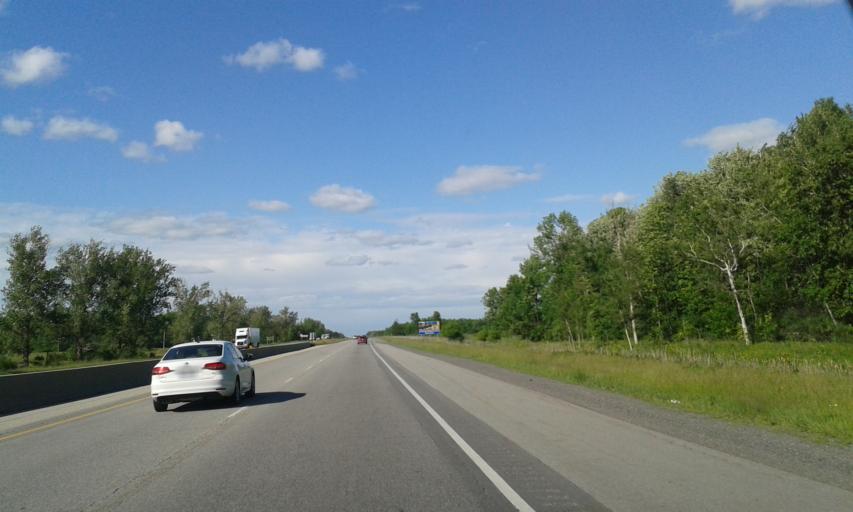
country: CA
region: Ontario
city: Brockville
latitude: 44.6589
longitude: -75.6184
